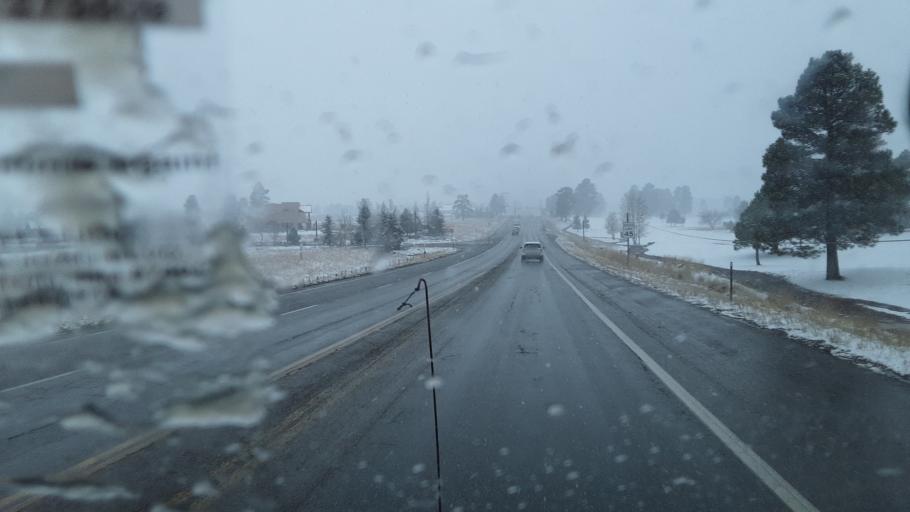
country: US
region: Colorado
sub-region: Archuleta County
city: Pagosa Springs
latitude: 37.2656
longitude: -107.0566
